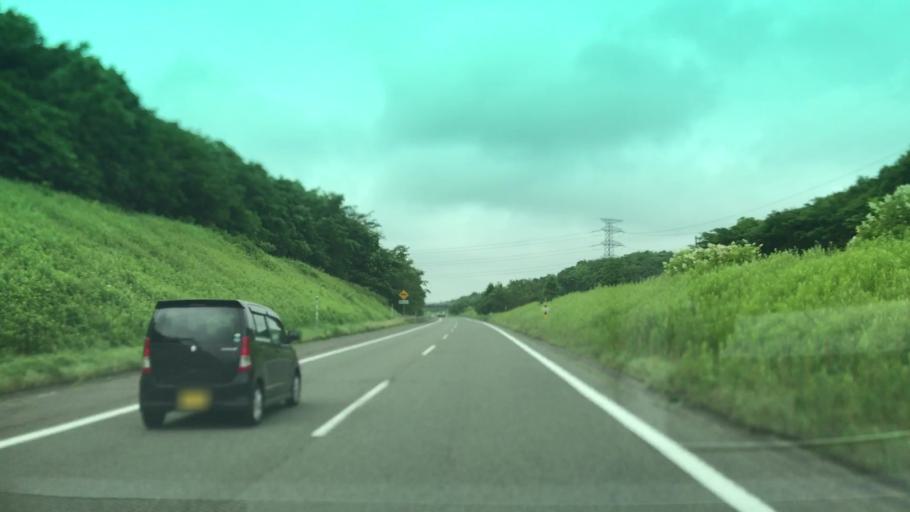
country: JP
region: Hokkaido
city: Chitose
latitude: 42.7346
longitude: 141.6525
